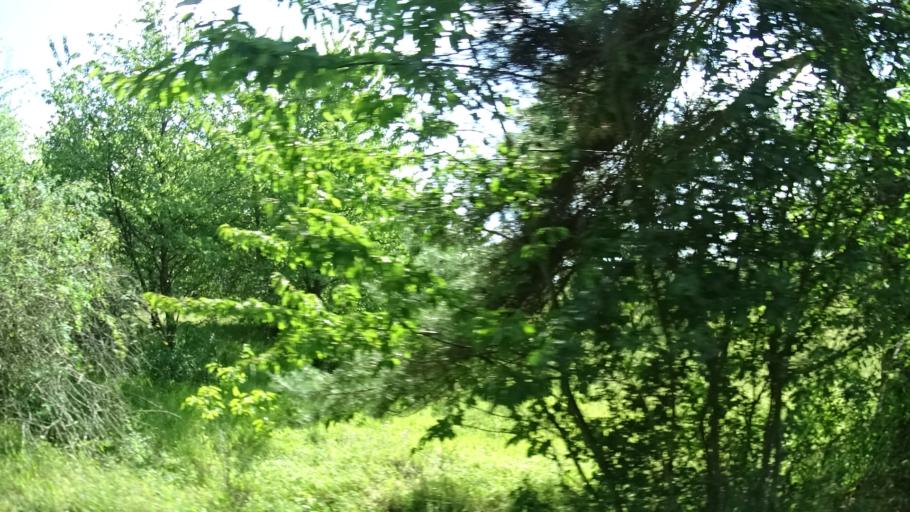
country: DE
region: Bavaria
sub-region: Regierungsbezirk Unterfranken
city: Trappstadt
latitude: 50.2843
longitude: 10.5887
